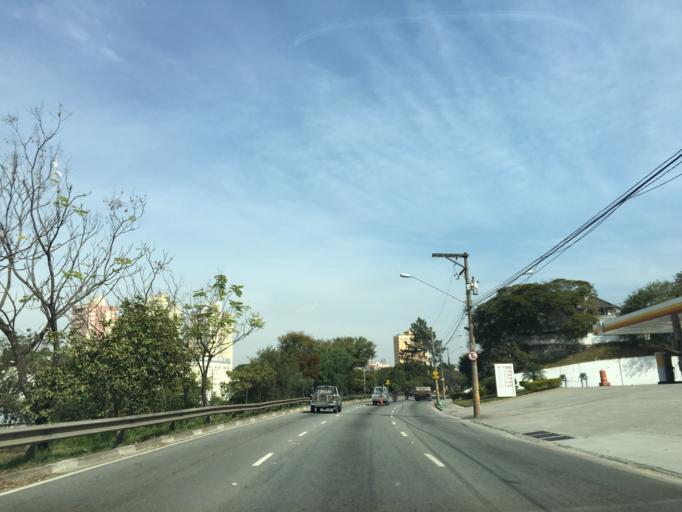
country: BR
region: Sao Paulo
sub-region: Osasco
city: Osasco
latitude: -23.5665
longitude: -46.7563
